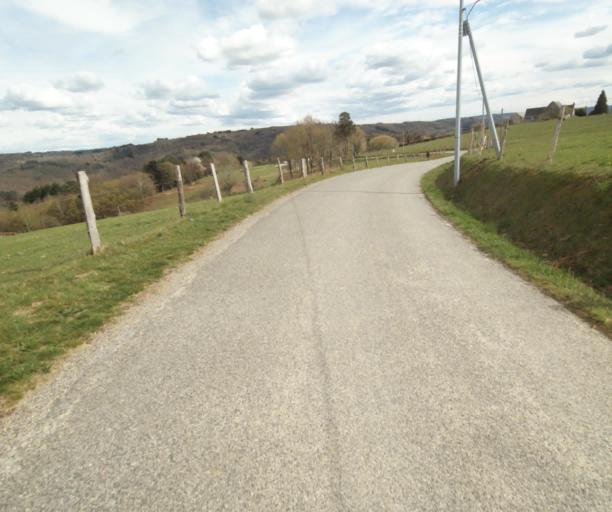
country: FR
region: Limousin
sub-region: Departement de la Correze
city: Argentat
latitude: 45.1811
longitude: 1.9438
